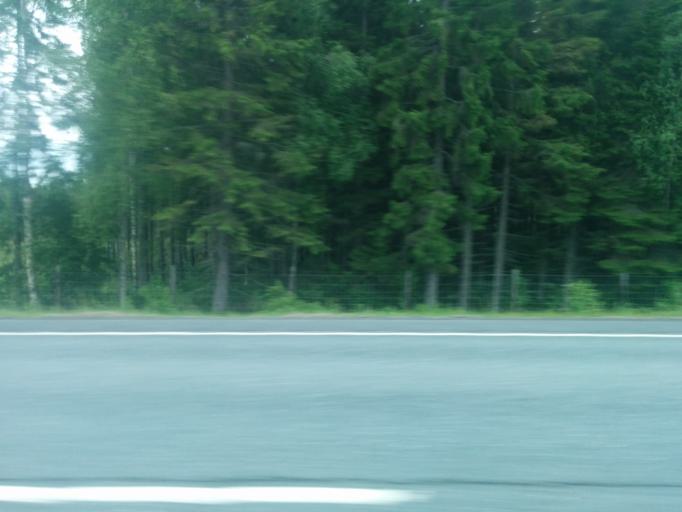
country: FI
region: Pirkanmaa
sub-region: Tampere
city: Orivesi
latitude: 61.6615
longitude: 24.2608
